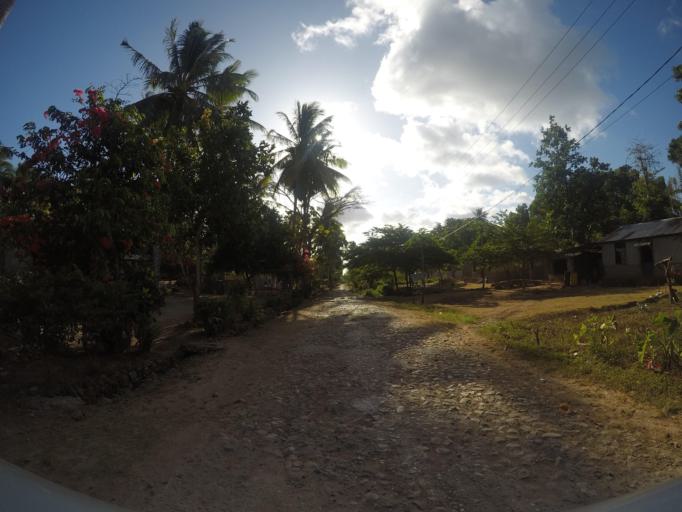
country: TL
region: Lautem
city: Lospalos
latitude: -8.4445
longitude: 126.8704
